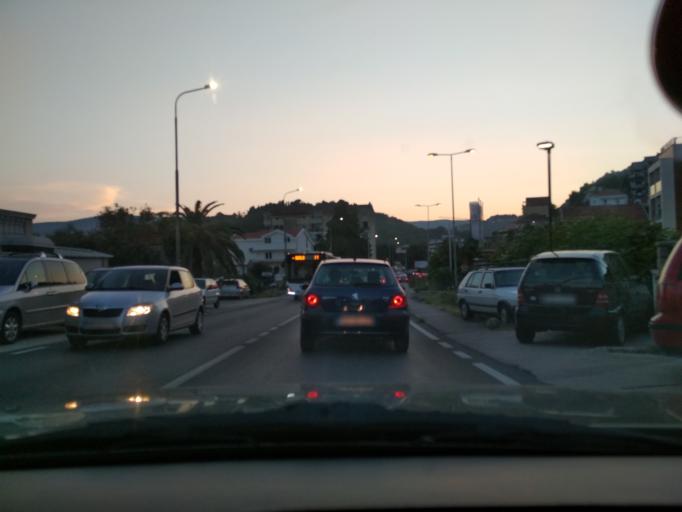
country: ME
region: Herceg Novi
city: Herceg-Novi
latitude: 42.4553
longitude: 18.5630
